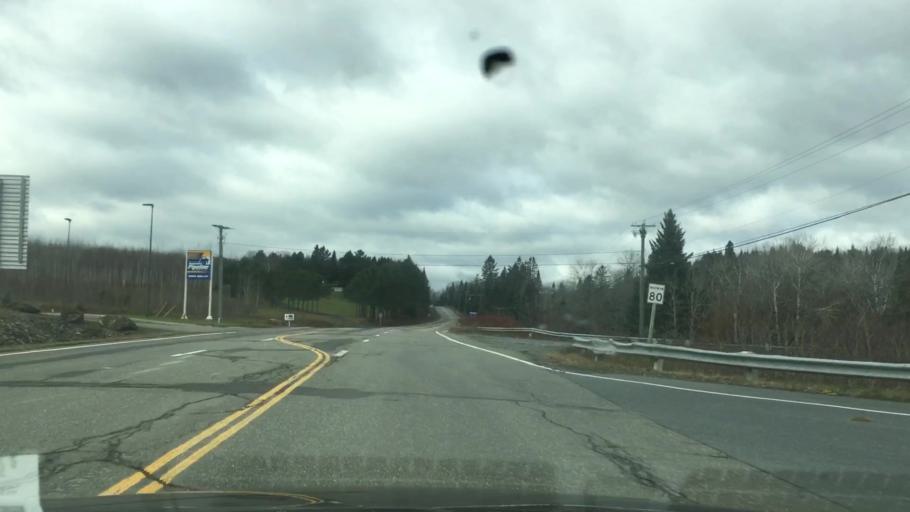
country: US
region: Maine
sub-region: Aroostook County
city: Fort Fairfield
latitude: 46.7495
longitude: -67.7188
